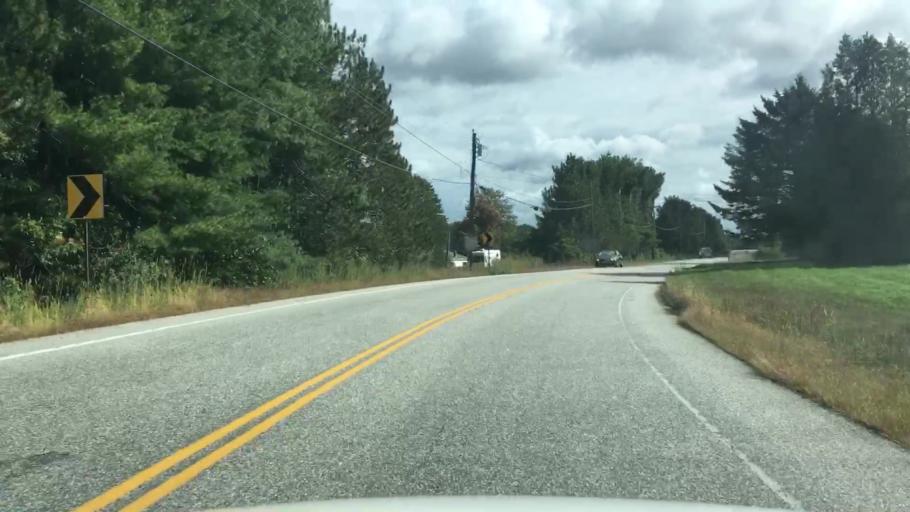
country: US
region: Maine
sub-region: Androscoggin County
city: Lisbon
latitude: 44.0208
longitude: -70.1757
